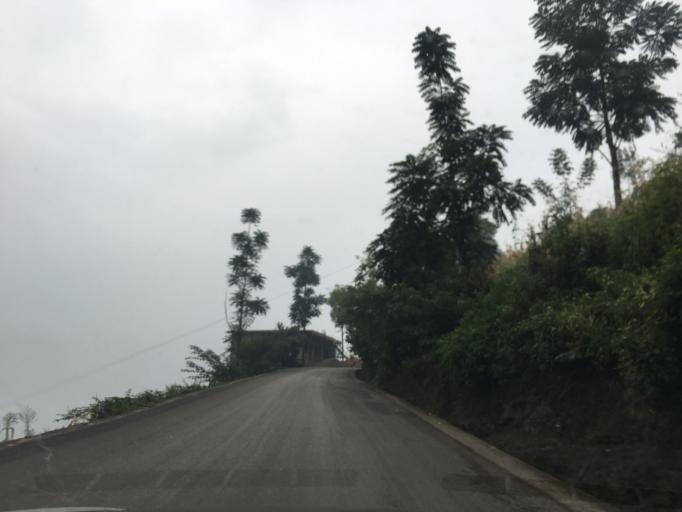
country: CN
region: Guizhou Sheng
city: Liupanshui
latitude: 26.0632
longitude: 105.1358
